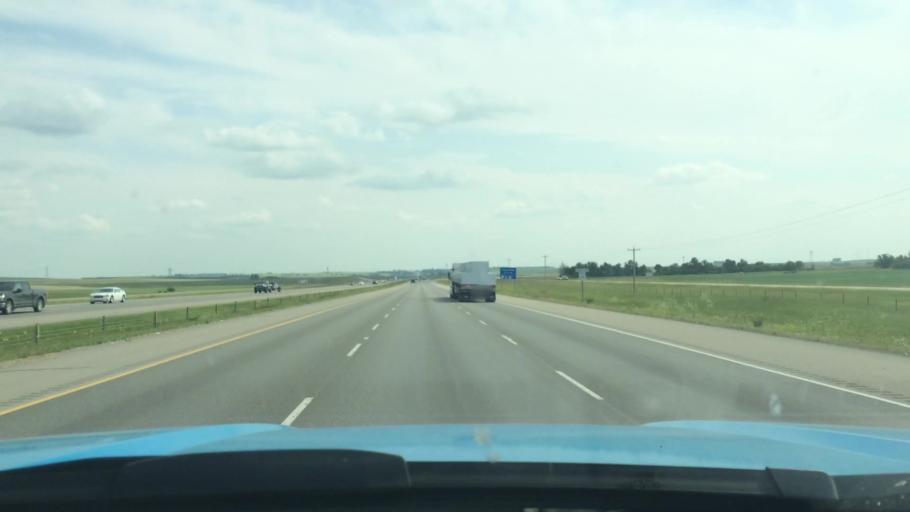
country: CA
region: Alberta
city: Crossfield
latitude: 51.4857
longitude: -114.0255
